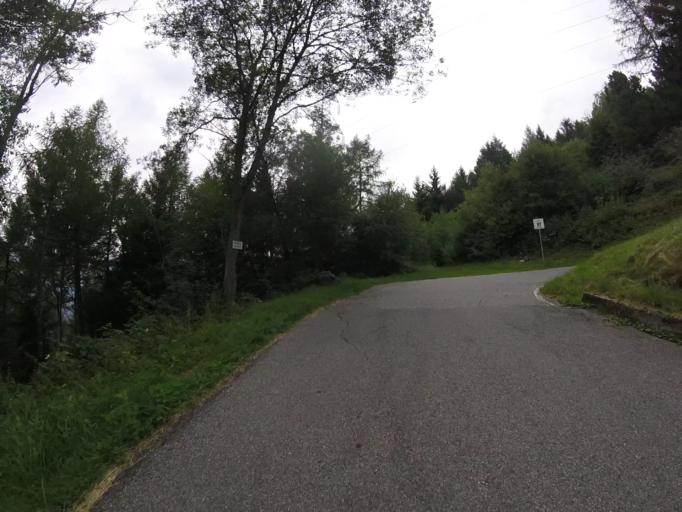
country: IT
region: Lombardy
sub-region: Provincia di Sondrio
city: Mazzo di Valtellina
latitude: 46.2590
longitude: 10.2895
